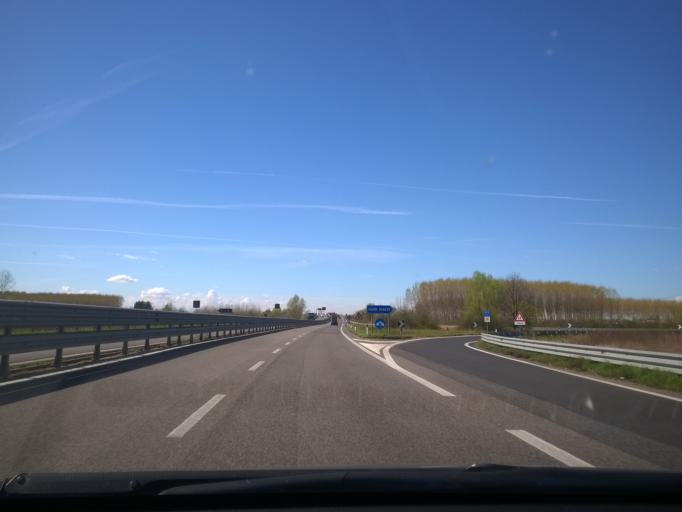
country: IT
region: Friuli Venezia Giulia
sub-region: Provincia di Pordenone
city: Fiume Veneto
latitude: 45.9374
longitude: 12.7191
